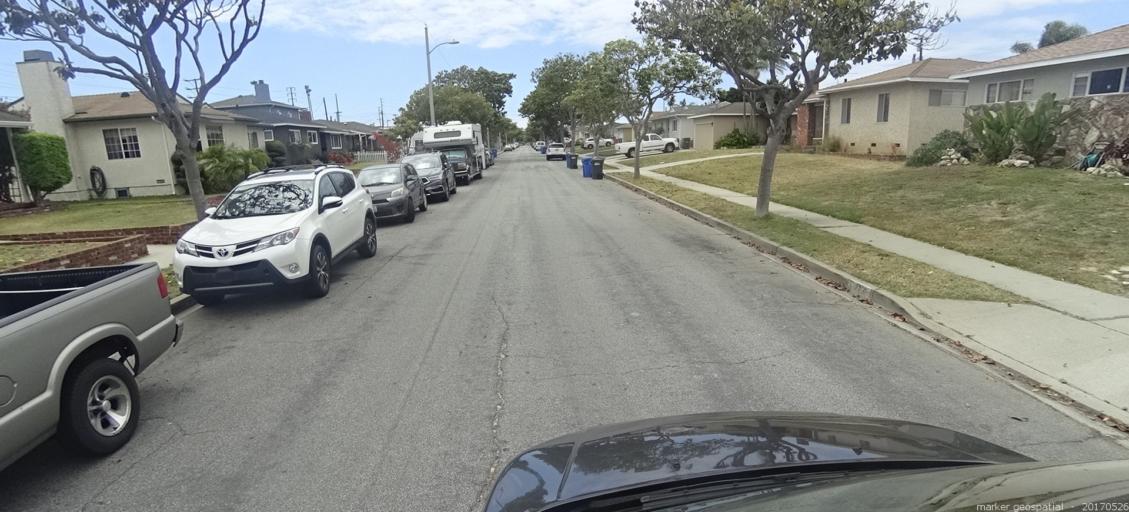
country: US
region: California
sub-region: Los Angeles County
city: Lawndale
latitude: 33.8591
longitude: -118.3582
